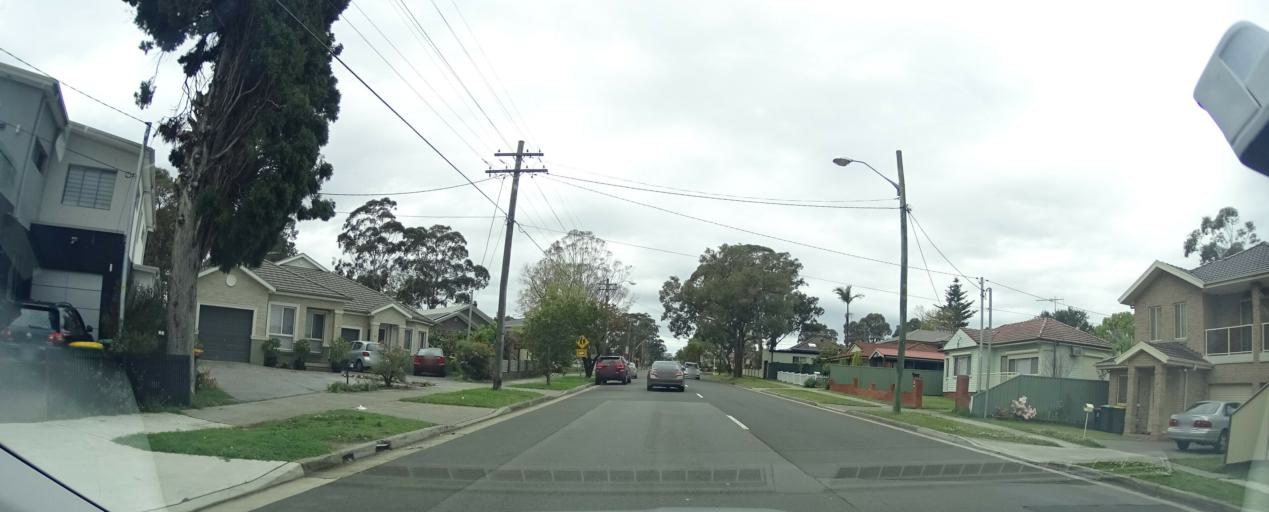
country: AU
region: New South Wales
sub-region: Bankstown
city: Revesby
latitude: -33.9564
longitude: 151.0228
